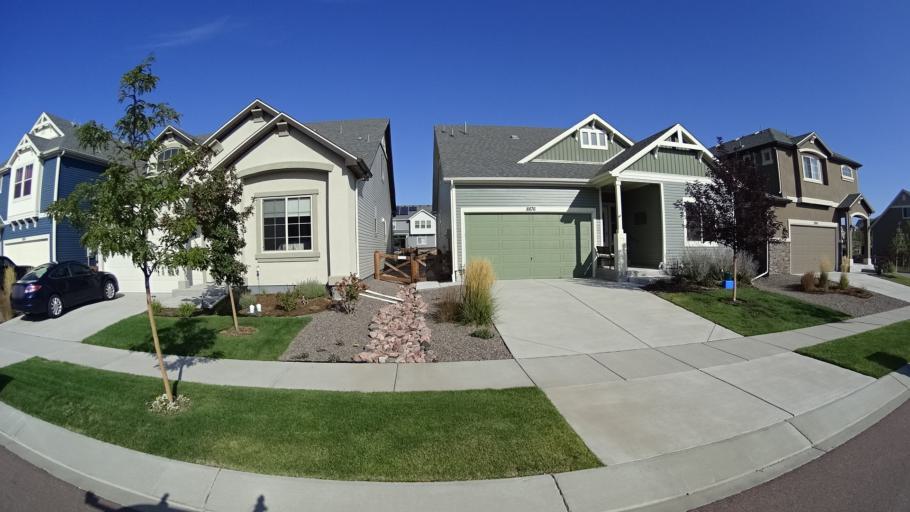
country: US
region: Colorado
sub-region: El Paso County
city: Cimarron Hills
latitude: 38.9322
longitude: -104.6704
